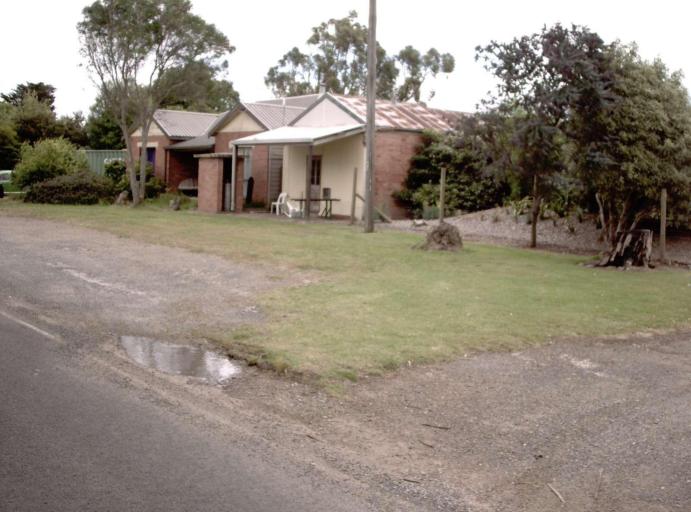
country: AU
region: Victoria
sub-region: Latrobe
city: Moe
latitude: -38.0135
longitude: 146.1496
